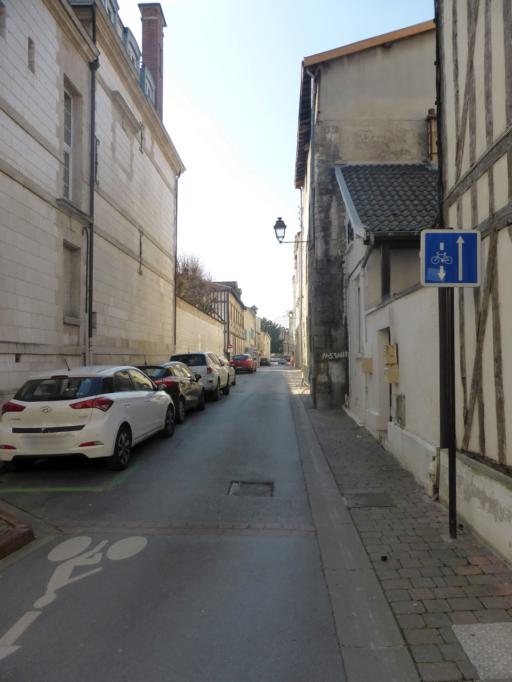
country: FR
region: Champagne-Ardenne
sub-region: Departement de la Marne
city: Chalons-en-Champagne
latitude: 48.9549
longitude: 4.3638
